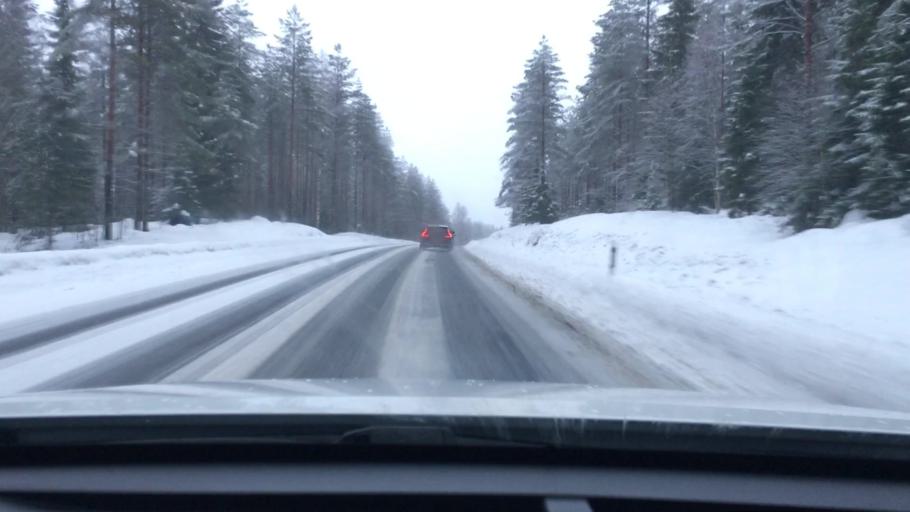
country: FI
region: Northern Savo
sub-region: Ylae-Savo
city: Sonkajaervi
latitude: 63.7665
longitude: 27.4124
